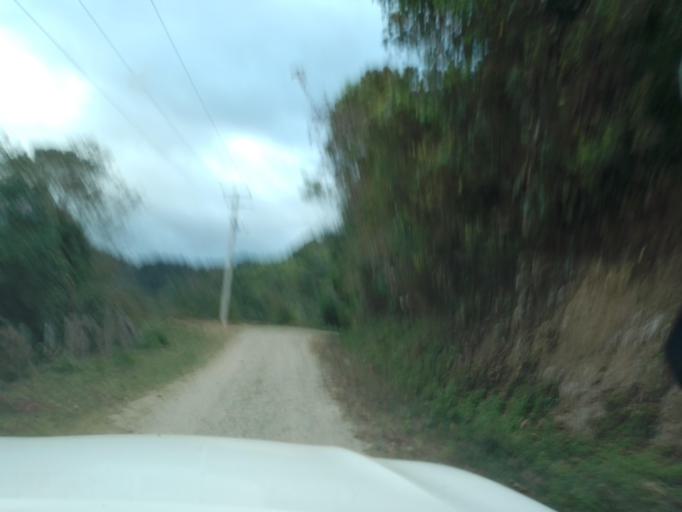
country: MX
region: Chiapas
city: Motozintla de Mendoza
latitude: 15.2148
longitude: -92.2283
